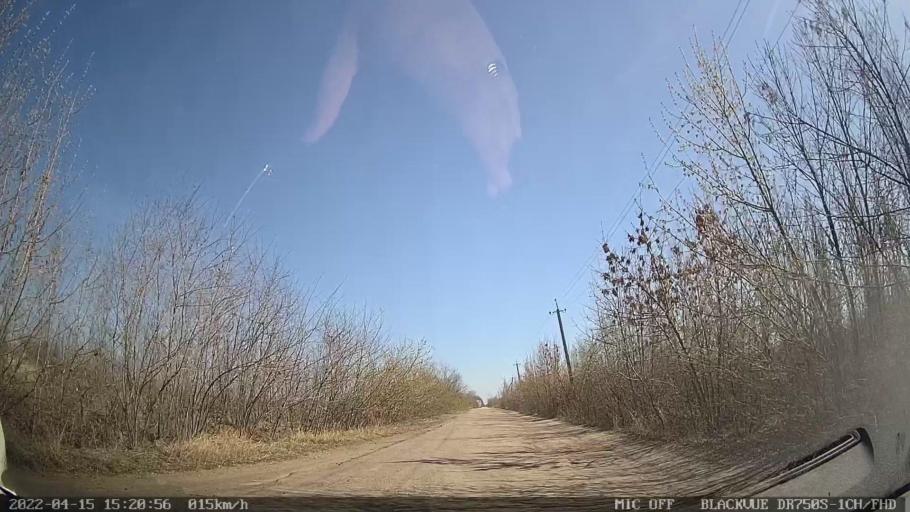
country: MD
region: Raionul Ocnita
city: Otaci
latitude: 48.3848
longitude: 27.9092
